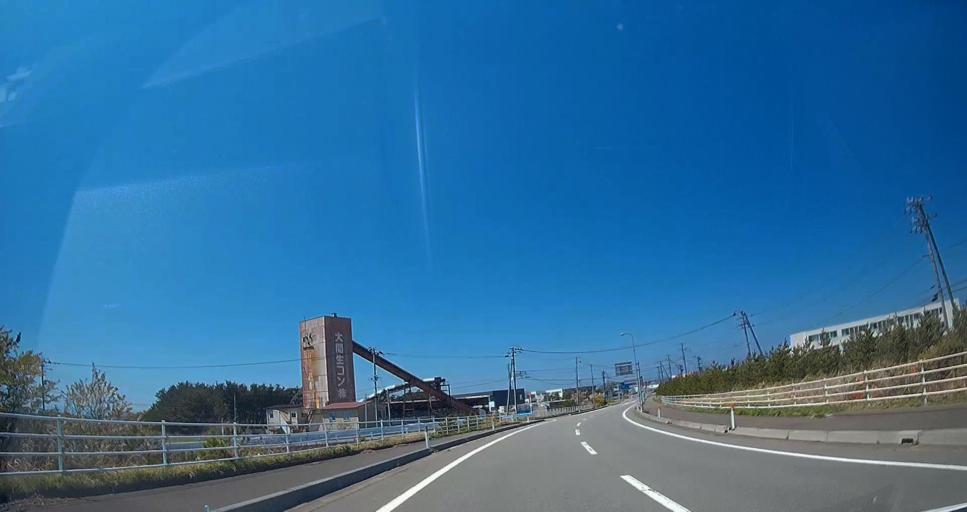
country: JP
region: Hokkaido
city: Hakodate
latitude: 41.5210
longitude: 140.9074
